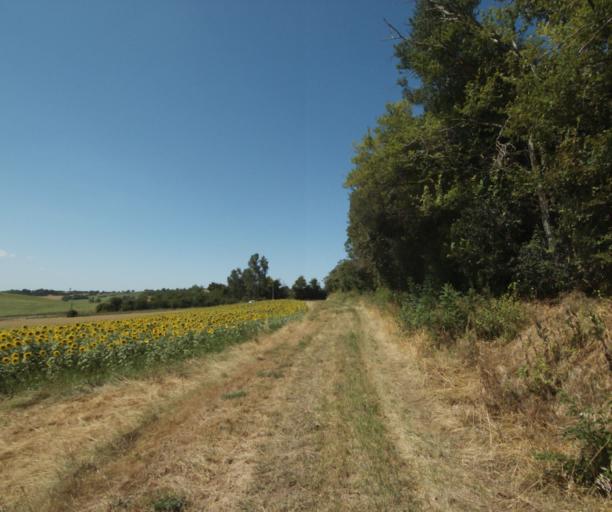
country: FR
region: Midi-Pyrenees
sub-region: Departement de la Haute-Garonne
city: Saint-Felix-Lauragais
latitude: 43.4903
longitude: 1.8928
